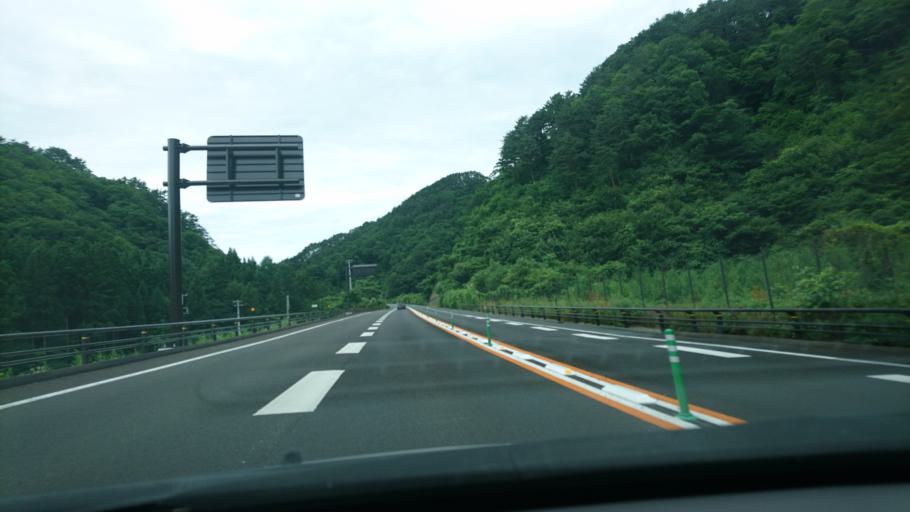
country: JP
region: Iwate
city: Miyako
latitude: 39.8443
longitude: 141.9528
